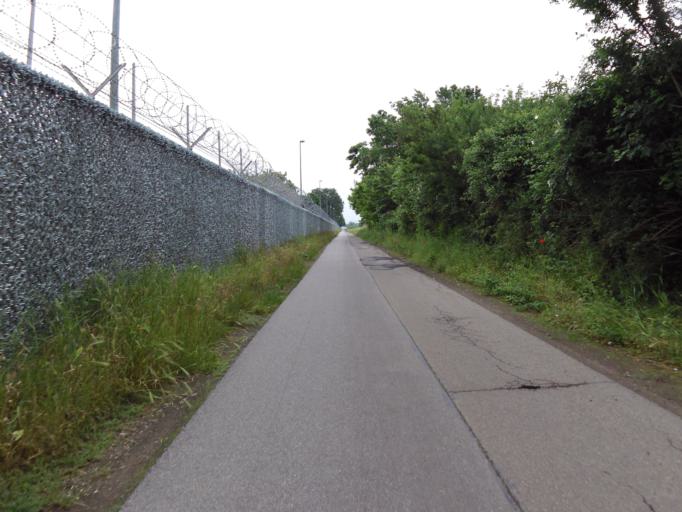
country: DE
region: Hesse
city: Lampertheim
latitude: 49.5555
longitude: 8.4538
